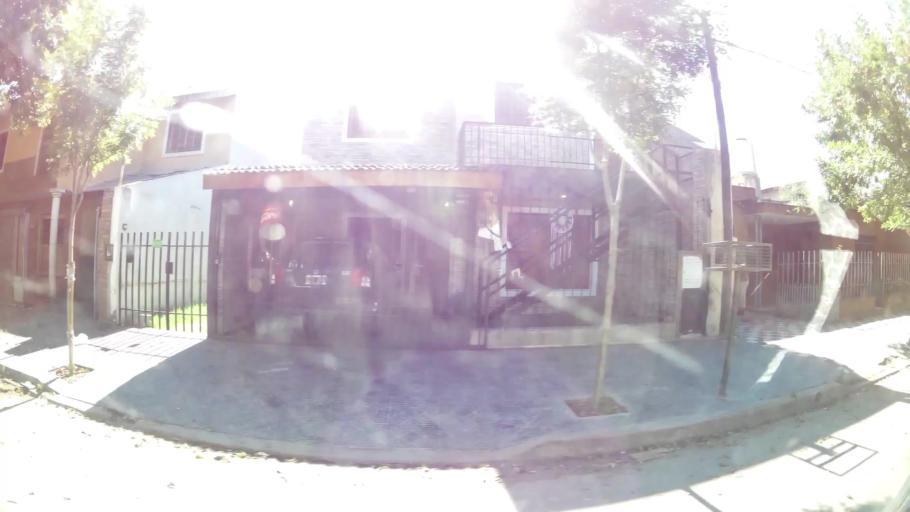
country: AR
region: Cordoba
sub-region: Departamento de Capital
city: Cordoba
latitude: -31.4376
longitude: -64.1498
